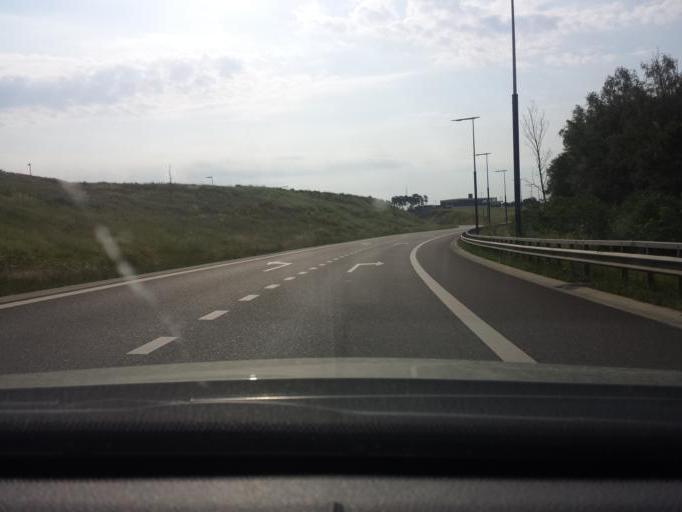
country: BE
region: Flanders
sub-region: Provincie Limburg
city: Lummen
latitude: 50.9985
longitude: 5.2193
